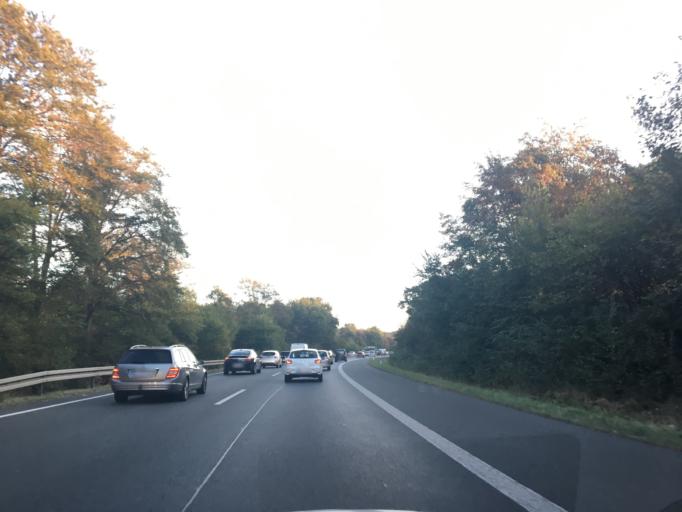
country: DE
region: Hesse
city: Raunheim
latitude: 50.0266
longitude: 8.4975
